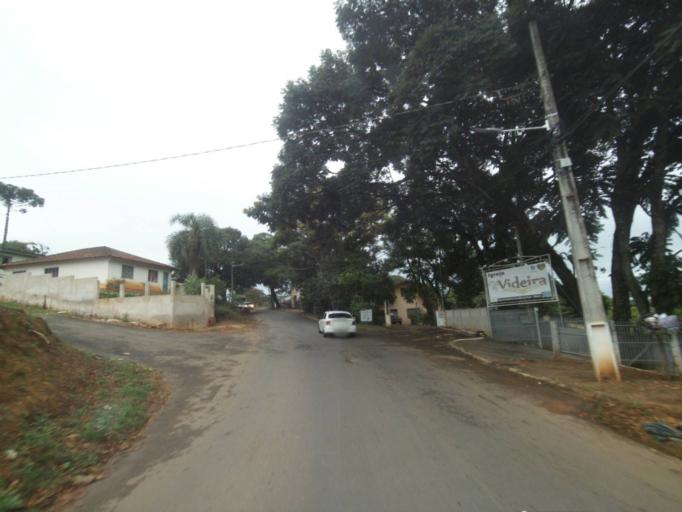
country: BR
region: Parana
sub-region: Telemaco Borba
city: Telemaco Borba
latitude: -24.3212
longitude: -50.6568
